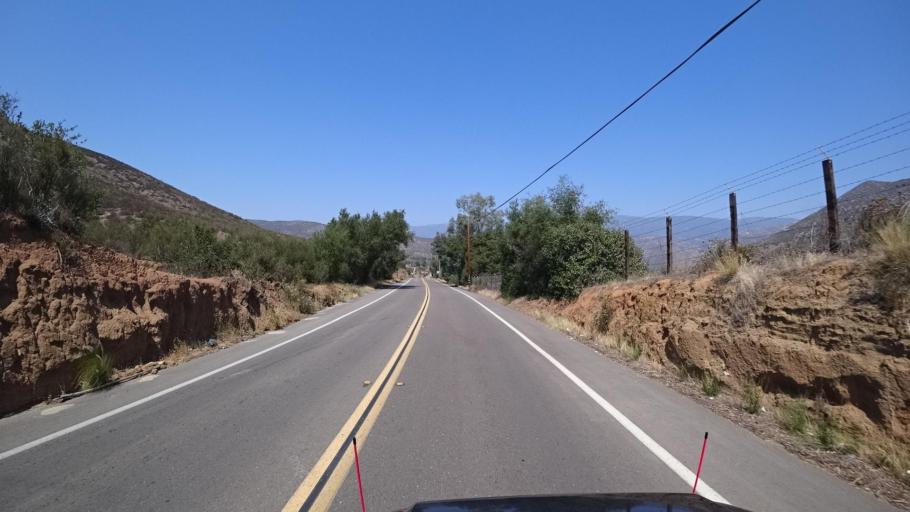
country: US
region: California
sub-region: San Diego County
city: Valley Center
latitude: 33.2398
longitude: -116.9643
